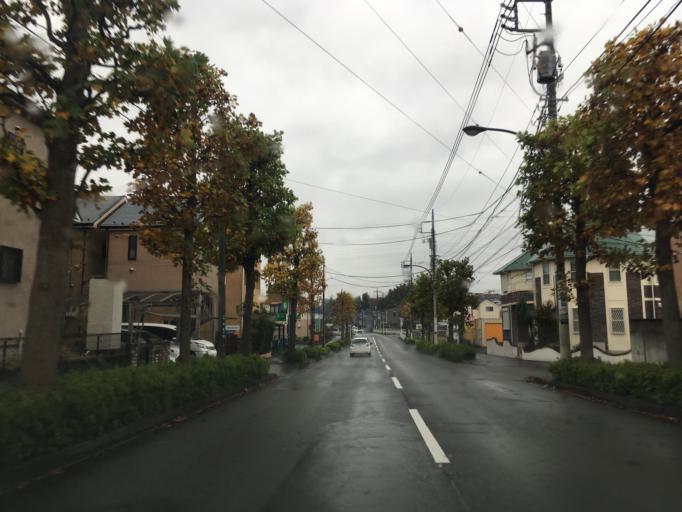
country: JP
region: Tokyo
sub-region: Machida-shi
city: Machida
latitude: 35.5770
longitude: 139.4038
